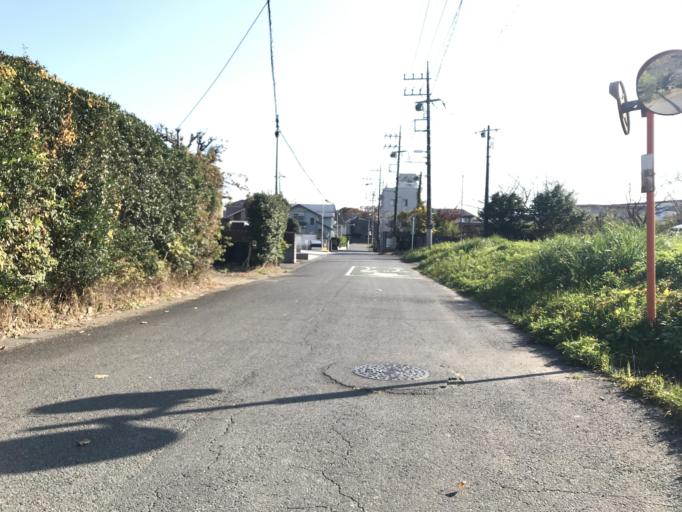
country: JP
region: Ibaraki
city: Ishioka
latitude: 36.1839
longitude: 140.2704
